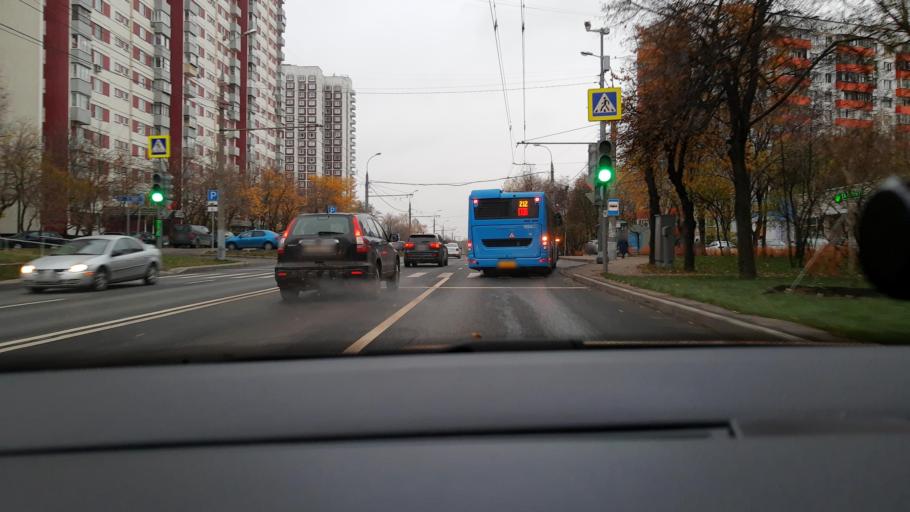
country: RU
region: Moscow
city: Strogino
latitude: 55.8506
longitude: 37.4111
